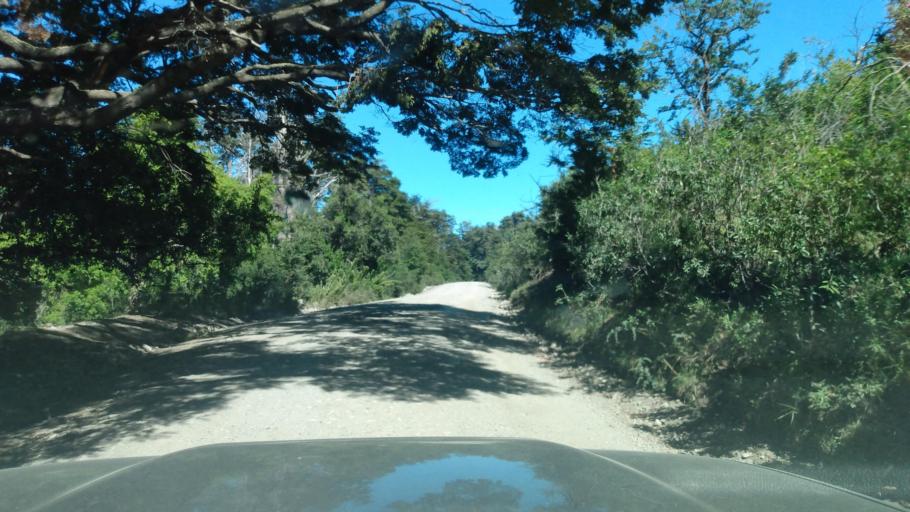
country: AR
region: Neuquen
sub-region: Departamento de Lacar
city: San Martin de los Andes
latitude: -39.7509
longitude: -71.4577
